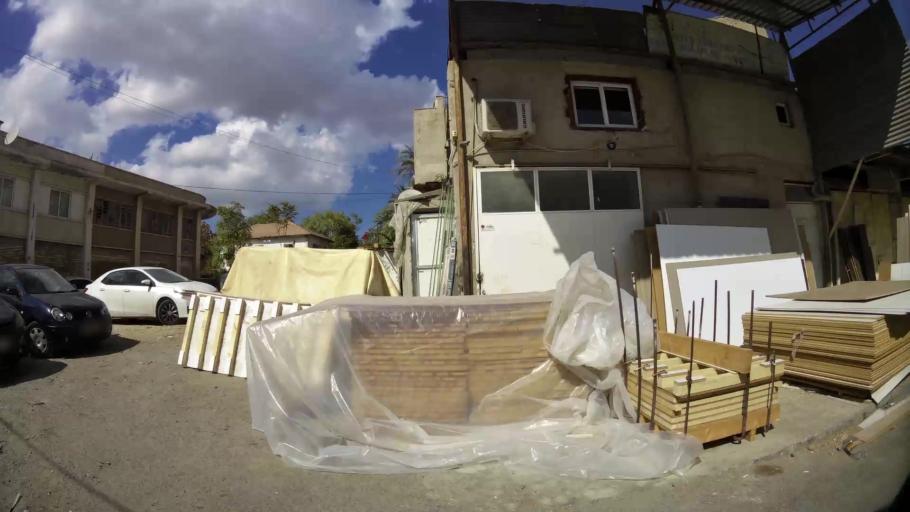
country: CY
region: Lefkosia
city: Nicosia
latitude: 35.1755
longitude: 33.3593
